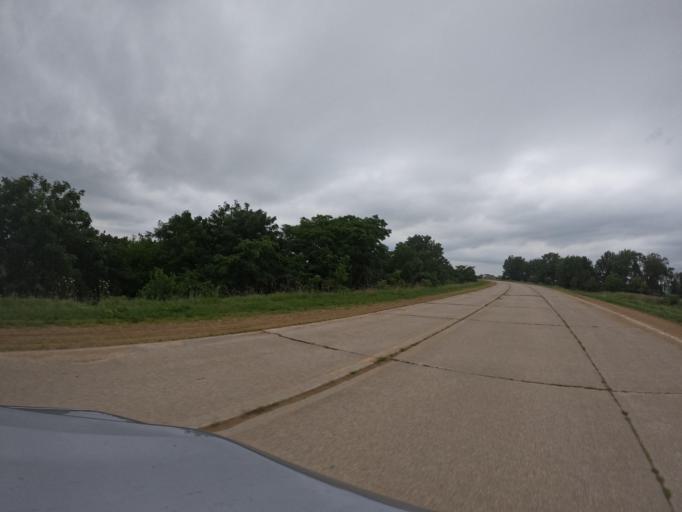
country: US
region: Iowa
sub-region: Jackson County
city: Maquoketa
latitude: 41.9467
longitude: -90.6226
